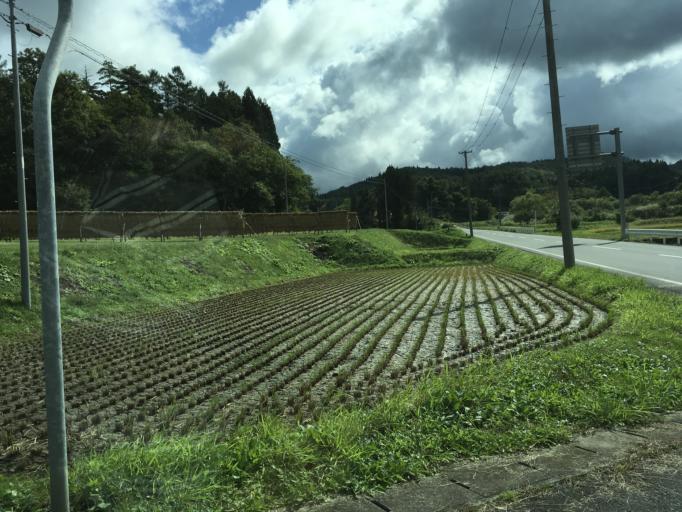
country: JP
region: Iwate
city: Ichinoseki
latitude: 38.8355
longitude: 141.3548
